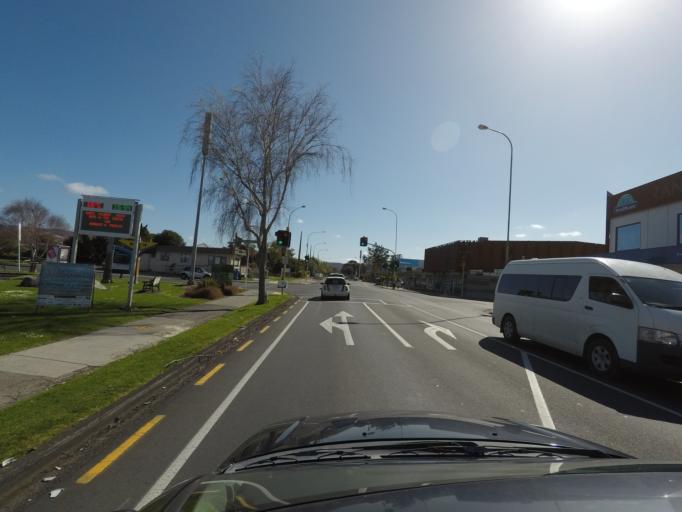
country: NZ
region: Auckland
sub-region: Auckland
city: Rosebank
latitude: -36.8639
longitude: 174.6028
